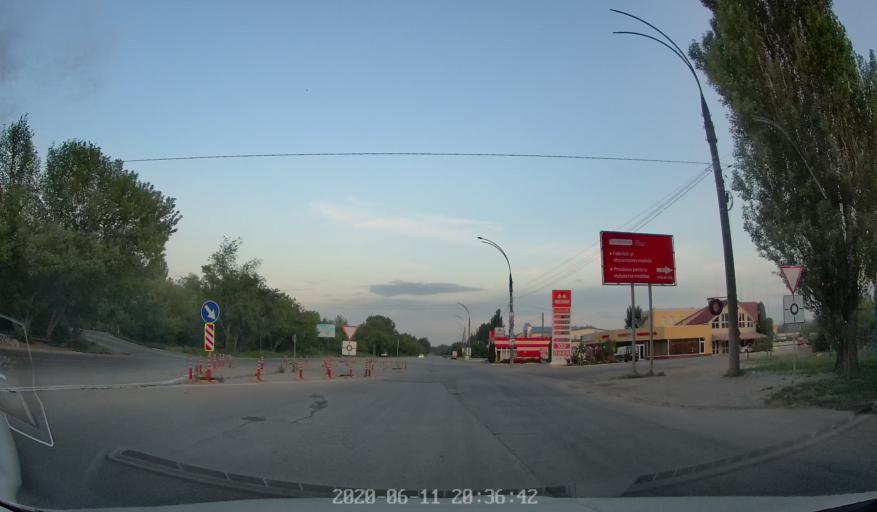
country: MD
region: Chisinau
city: Chisinau
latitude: 47.0097
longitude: 28.8740
